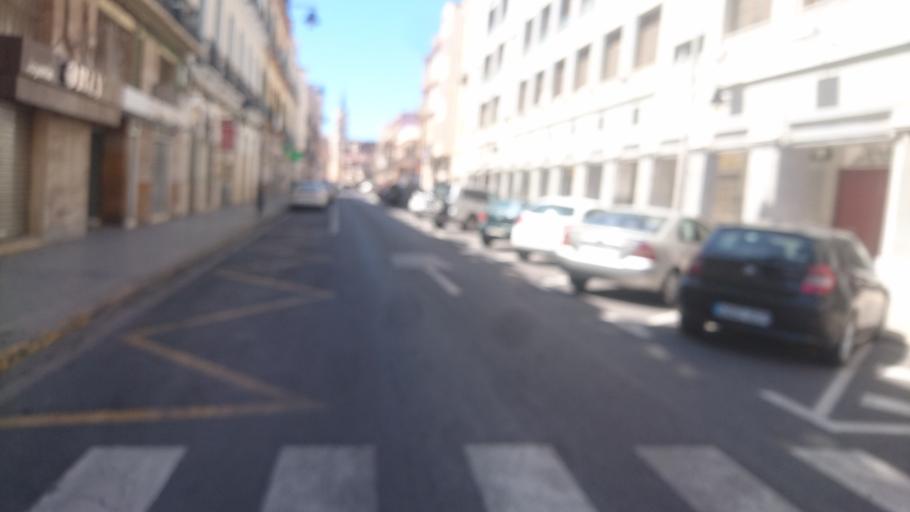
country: ES
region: Melilla
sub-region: Melilla
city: Melilla
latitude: 35.2931
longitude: -2.9384
